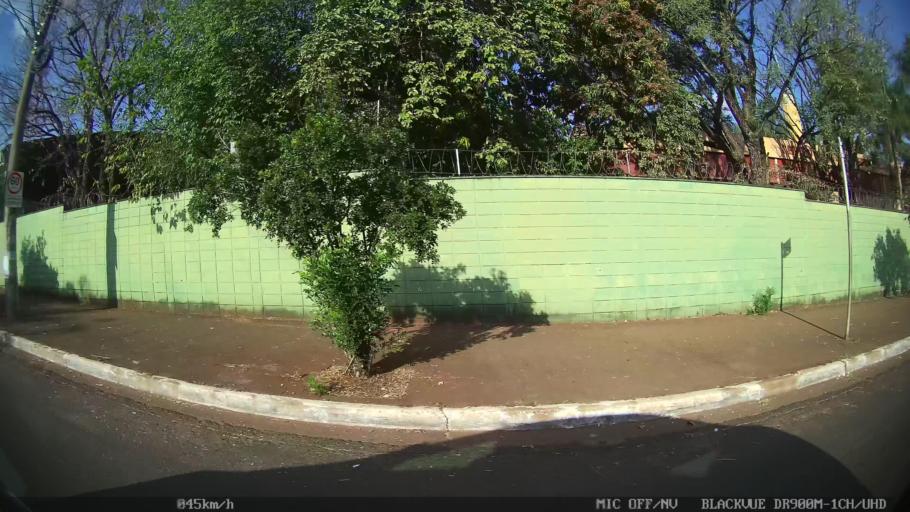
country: BR
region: Sao Paulo
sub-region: Ribeirao Preto
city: Ribeirao Preto
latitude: -21.1393
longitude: -47.7981
